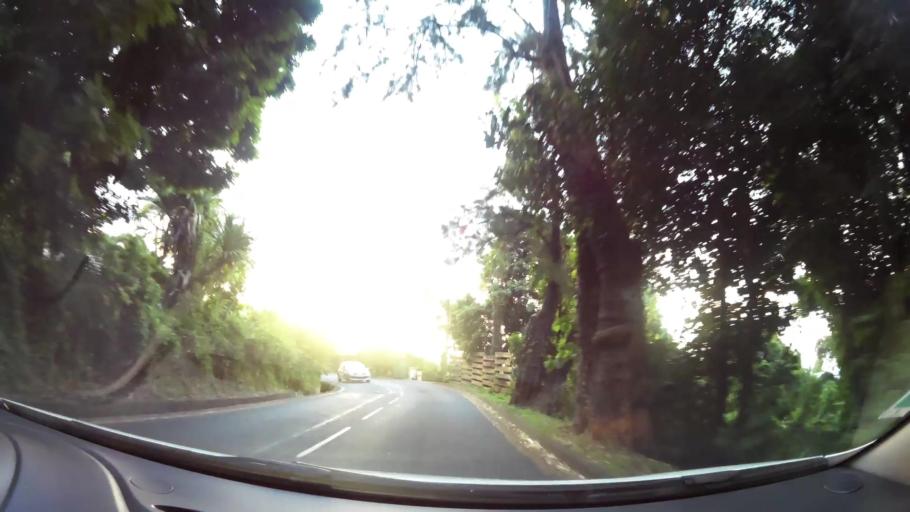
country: RE
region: Reunion
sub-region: Reunion
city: Saint-Denis
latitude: -20.9144
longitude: 55.4612
